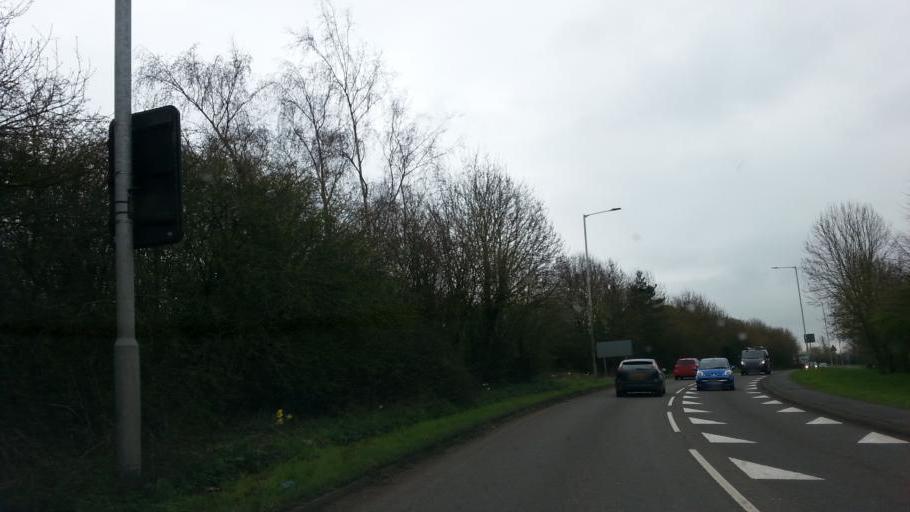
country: GB
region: England
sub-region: Leicestershire
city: Anstey
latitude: 52.6693
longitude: -1.1832
